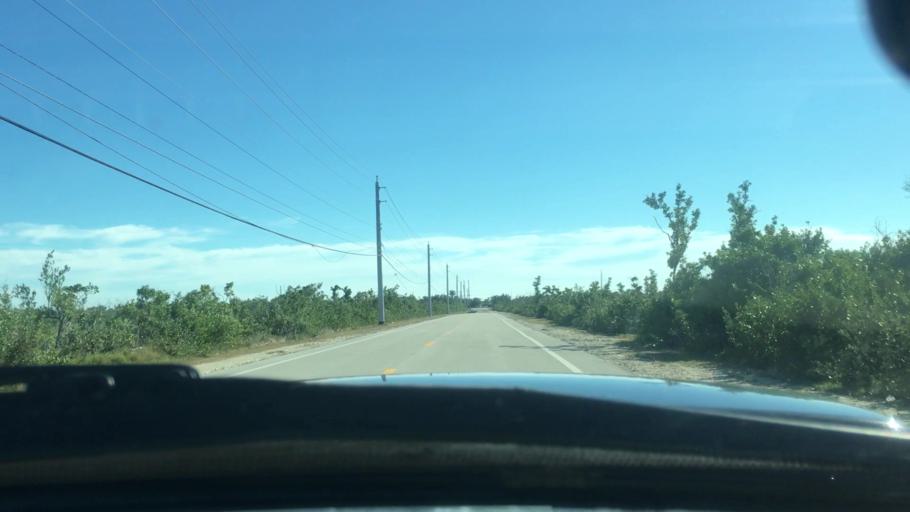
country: US
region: Florida
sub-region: Monroe County
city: Cudjoe Key
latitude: 24.6719
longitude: -81.4997
